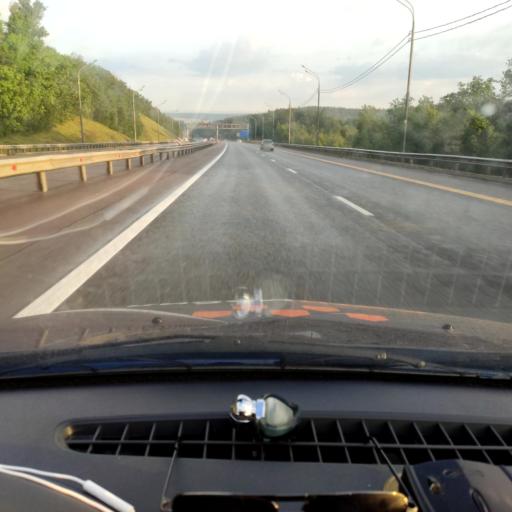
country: RU
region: Lipetsk
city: Zadonsk
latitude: 52.3636
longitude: 38.9317
